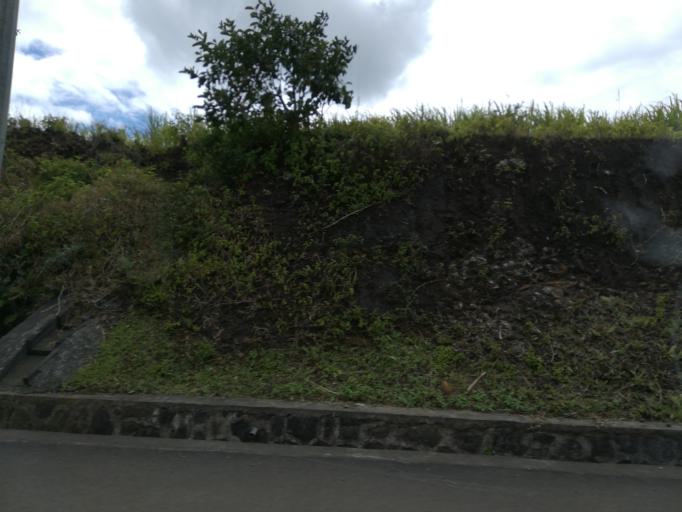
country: MU
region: Moka
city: Providence
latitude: -20.2438
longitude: 57.6022
